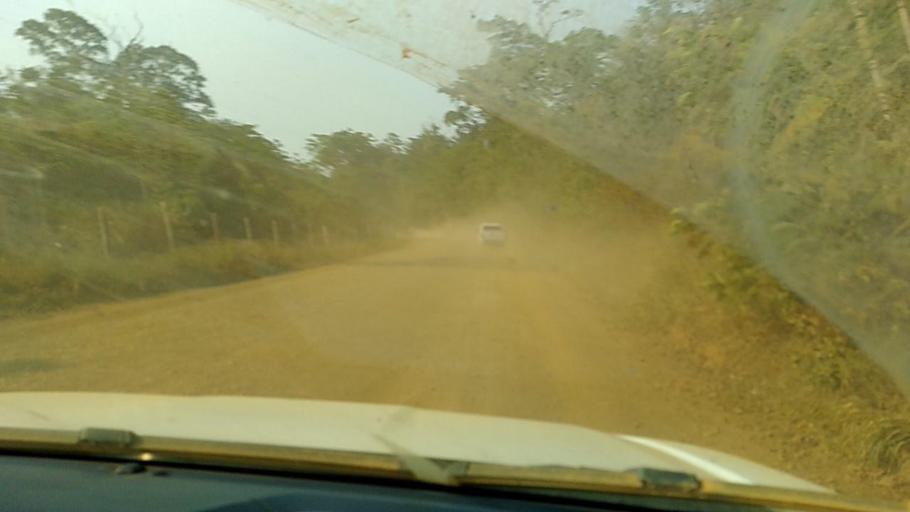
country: BR
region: Rondonia
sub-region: Porto Velho
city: Porto Velho
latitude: -8.7498
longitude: -63.9643
